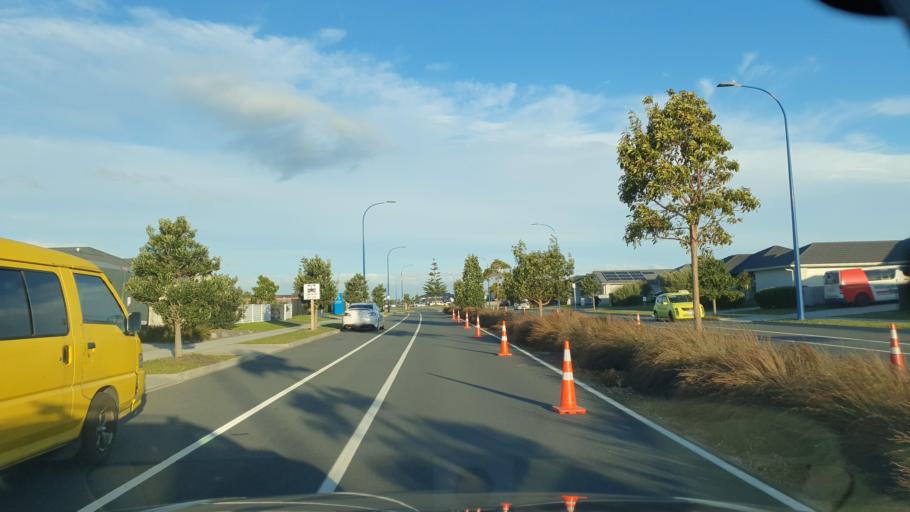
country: NZ
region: Bay of Plenty
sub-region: Western Bay of Plenty District
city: Maketu
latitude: -37.7245
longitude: 176.3394
